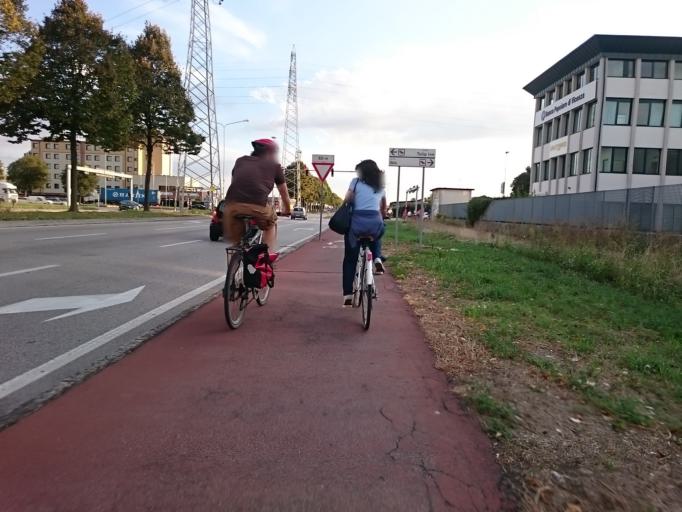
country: IT
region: Veneto
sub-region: Provincia di Padova
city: Noventa
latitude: 45.3924
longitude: 11.9446
